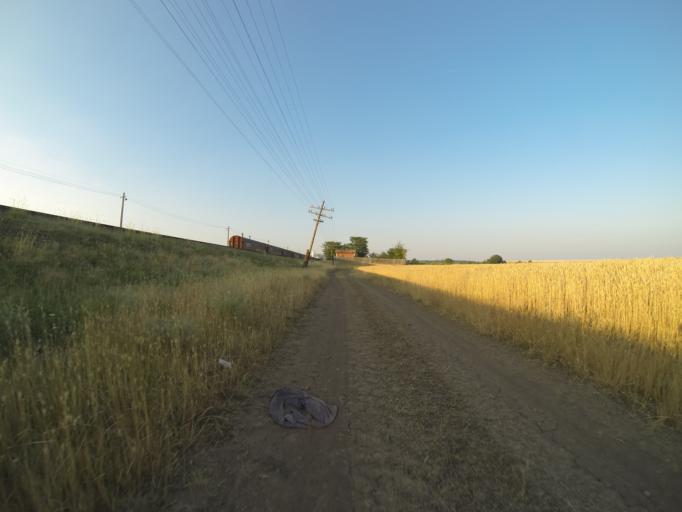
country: RO
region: Dolj
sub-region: Comuna Segarcea
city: Segarcea
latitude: 44.0788
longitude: 23.7202
